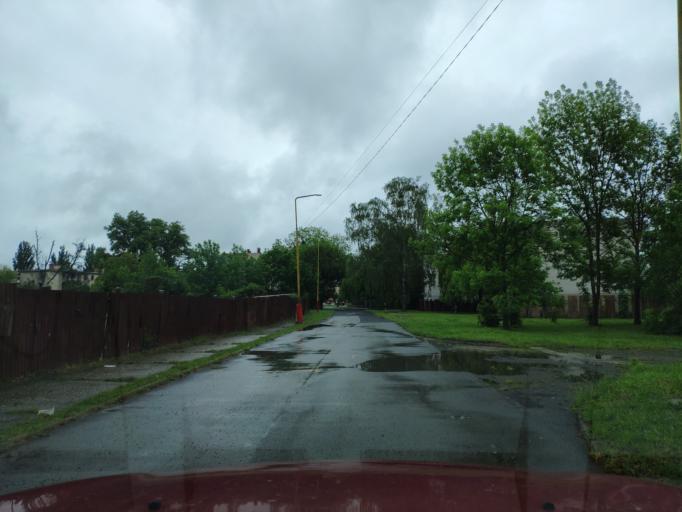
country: SK
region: Kosicky
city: Cierna nad Tisou
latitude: 48.4139
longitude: 22.0847
